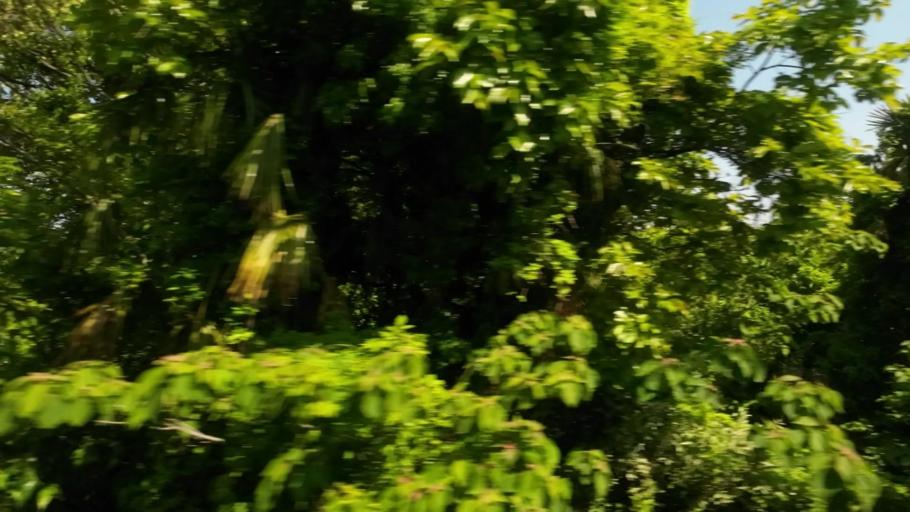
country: JP
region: Ehime
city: Kawanoecho
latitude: 33.9697
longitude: 133.4720
